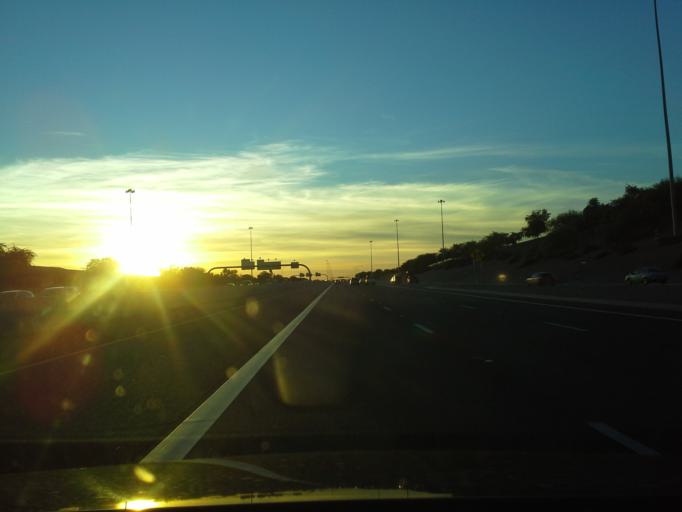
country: US
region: Arizona
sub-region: Pinal County
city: Apache Junction
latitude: 33.3868
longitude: -111.6513
